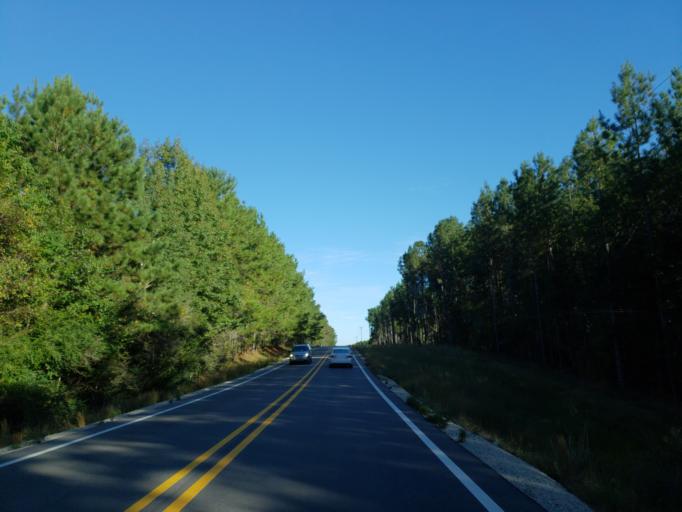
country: US
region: Mississippi
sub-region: Perry County
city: Richton
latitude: 31.3685
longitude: -89.0665
